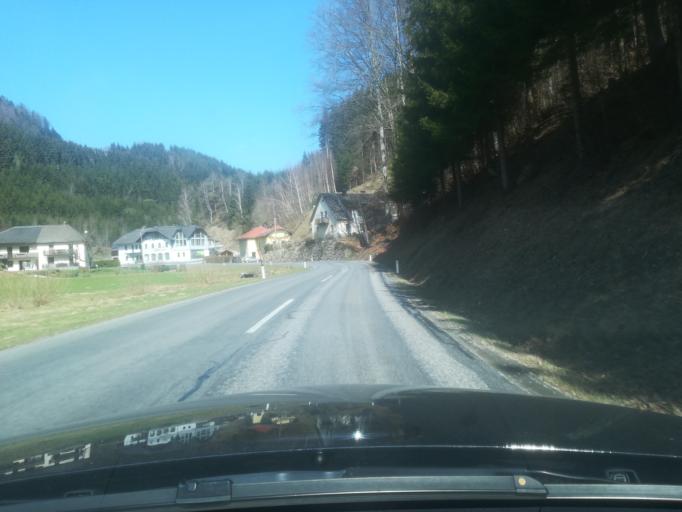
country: AT
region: Upper Austria
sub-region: Politischer Bezirk Perg
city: Sankt Georgen am Walde
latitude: 48.4448
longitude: 14.7829
